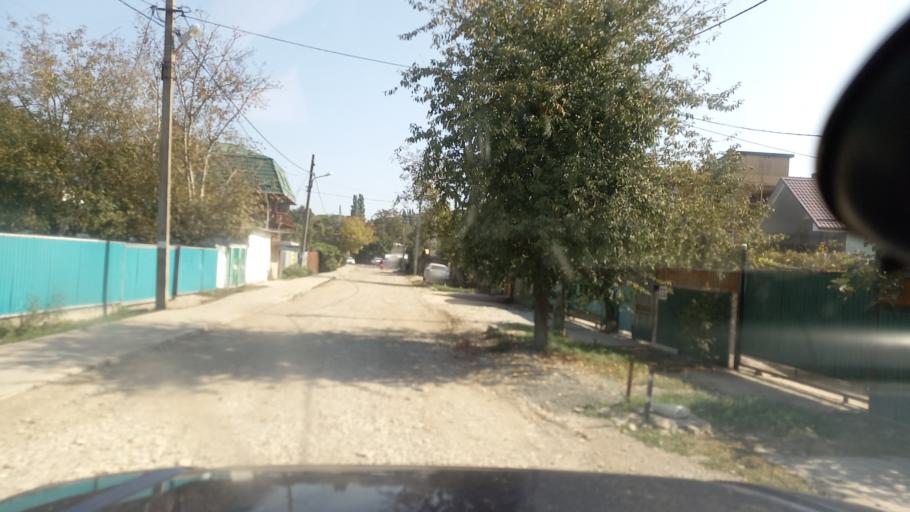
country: RU
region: Krasnodarskiy
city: Arkhipo-Osipovka
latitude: 44.3650
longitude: 38.5272
